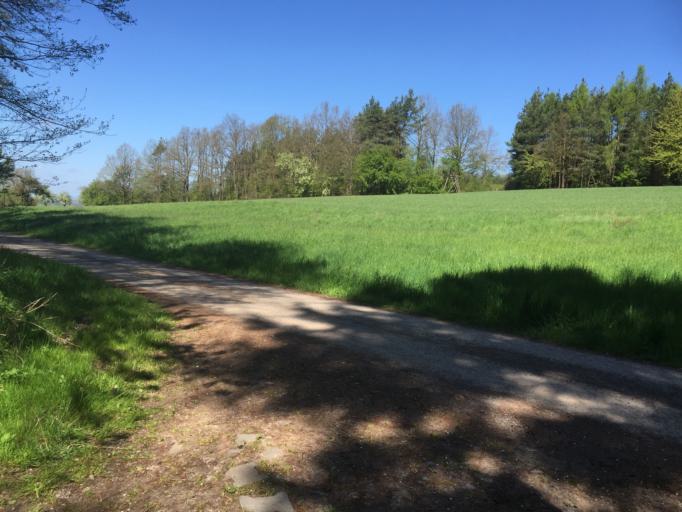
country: DE
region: Bavaria
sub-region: Regierungsbezirk Unterfranken
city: Sulzfeld
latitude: 50.2607
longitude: 10.4200
